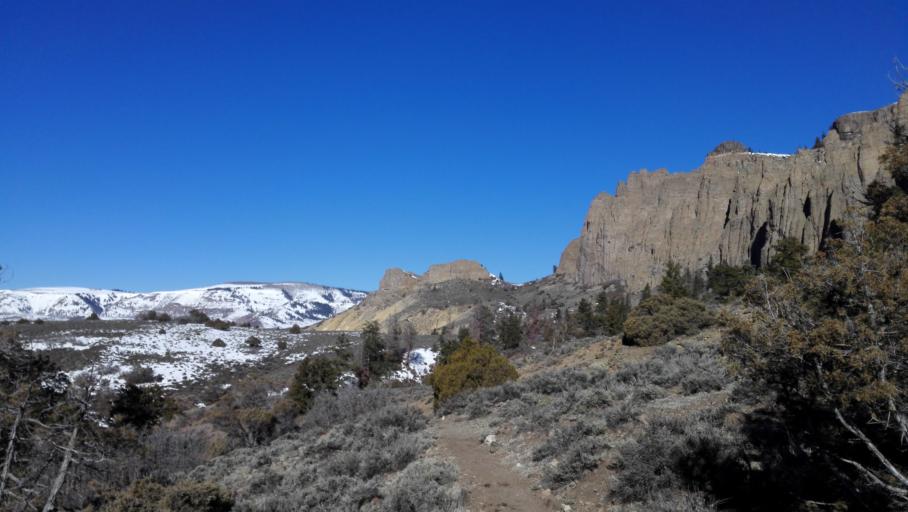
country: US
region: Colorado
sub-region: Gunnison County
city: Gunnison
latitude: 38.4818
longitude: -107.2647
